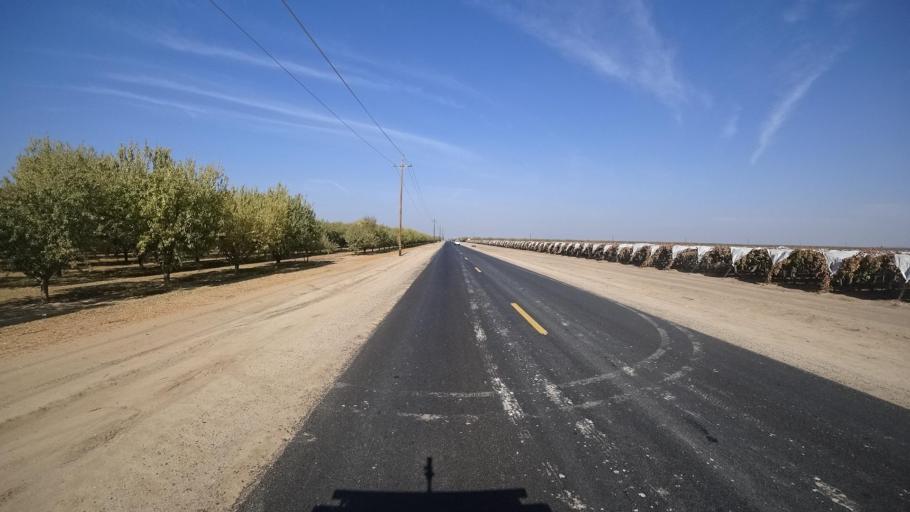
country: US
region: California
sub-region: Kern County
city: Shafter
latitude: 35.5106
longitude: -119.1521
